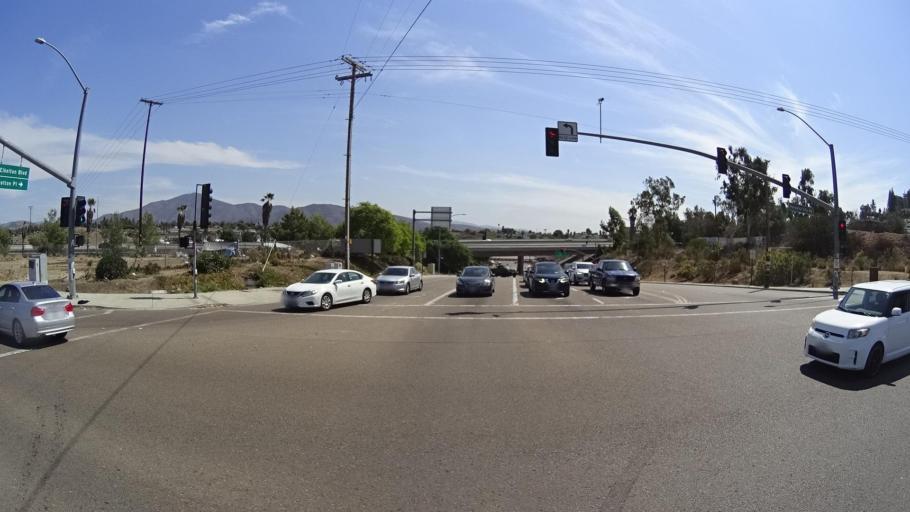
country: US
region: California
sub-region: San Diego County
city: La Presa
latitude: 32.7027
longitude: -117.0126
